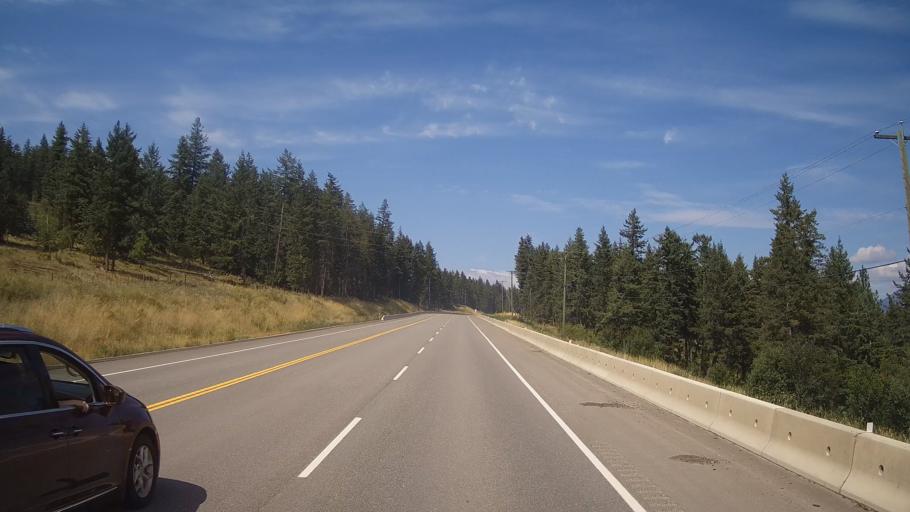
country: CA
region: British Columbia
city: Kamloops
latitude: 51.2718
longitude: -120.1776
